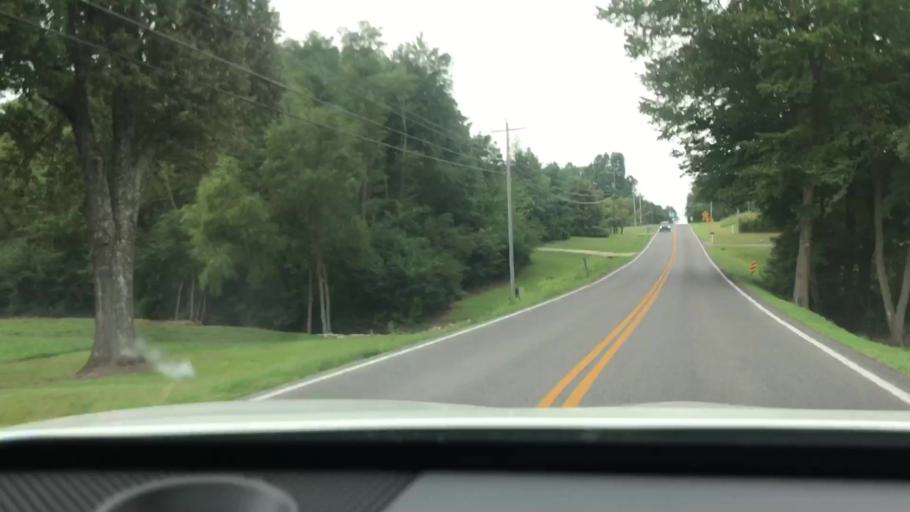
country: US
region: Kentucky
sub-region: Calloway County
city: Murray
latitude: 36.6808
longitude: -88.3004
